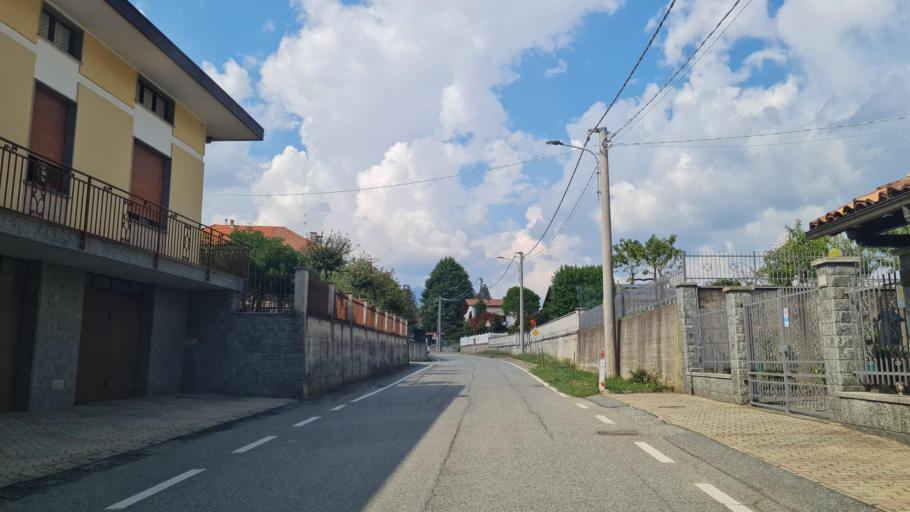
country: IT
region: Piedmont
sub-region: Provincia di Biella
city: Lessona
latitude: 45.5870
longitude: 8.1823
